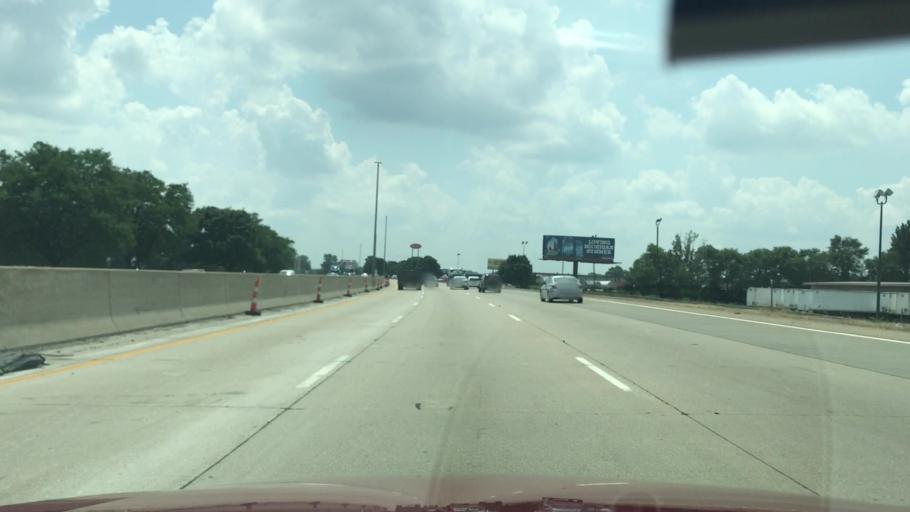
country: US
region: Michigan
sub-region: Kent County
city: Kentwood
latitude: 42.8805
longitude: -85.6819
